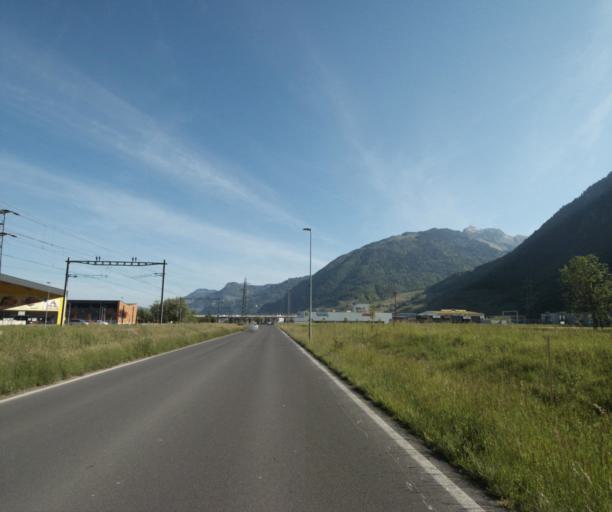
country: CH
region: Vaud
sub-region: Aigle District
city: Villeneuve
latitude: 46.3823
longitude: 6.9289
